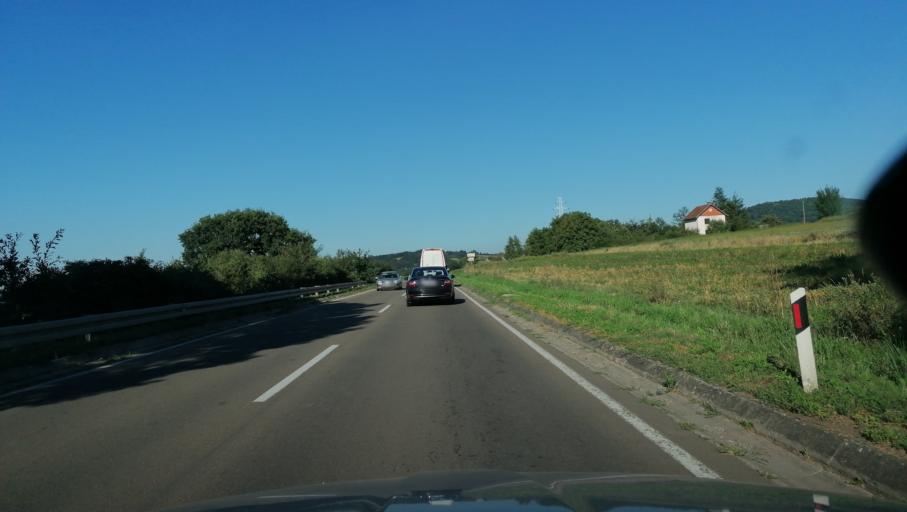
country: RS
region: Central Serbia
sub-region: Sumadijski Okrug
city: Knic
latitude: 43.9210
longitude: 20.6691
